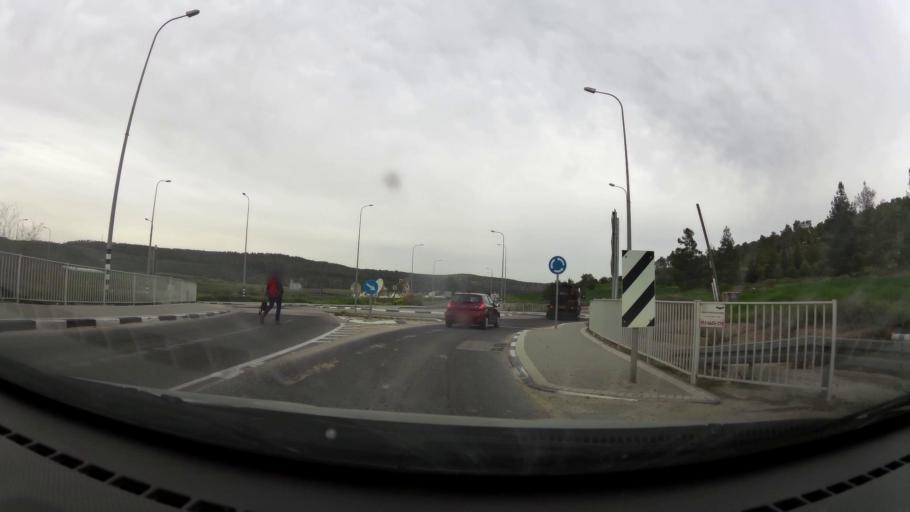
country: IL
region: Jerusalem
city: Bet Shemesh
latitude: 31.6836
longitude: 35.0021
